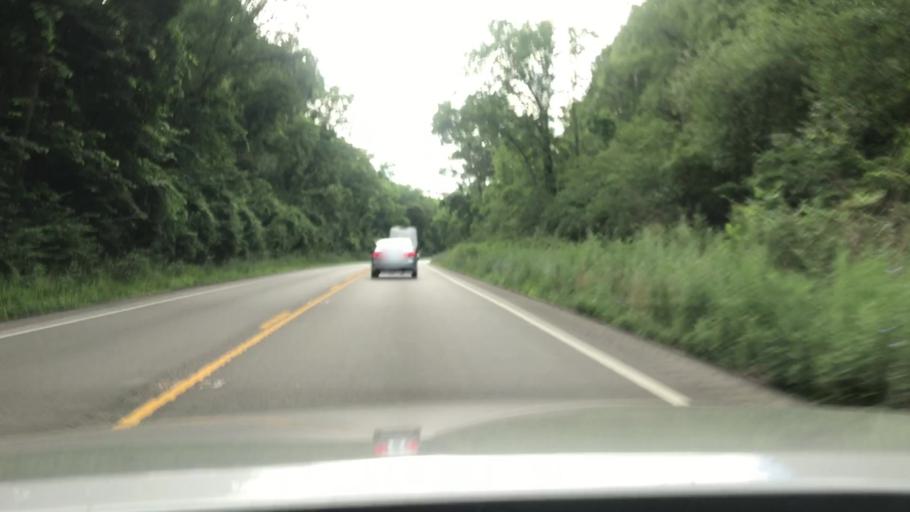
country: US
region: Illinois
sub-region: DuPage County
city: Burr Ridge
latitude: 41.7047
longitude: -87.9242
